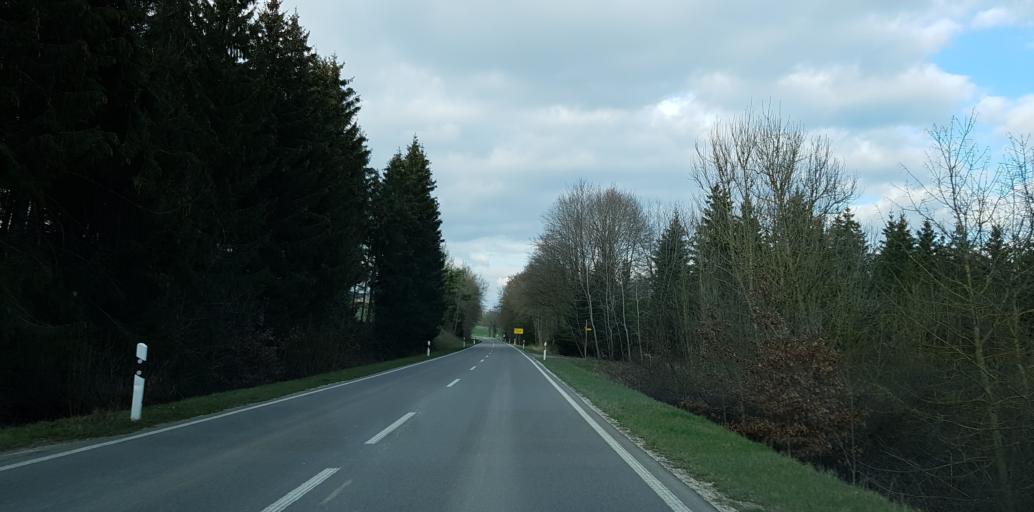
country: DE
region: Baden-Wuerttemberg
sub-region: Tuebingen Region
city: Erbach
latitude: 48.3506
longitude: 9.8544
